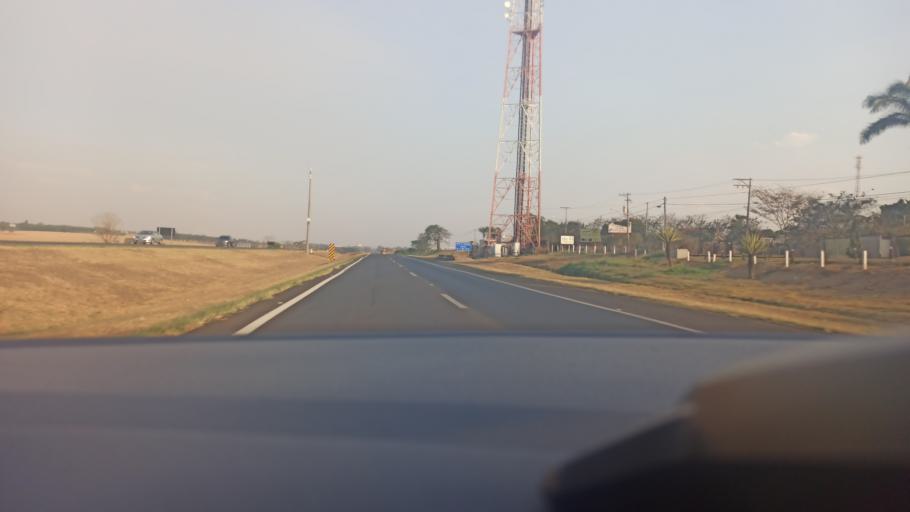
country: BR
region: Sao Paulo
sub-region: Sao Jose Do Rio Preto
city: Sao Jose do Rio Preto
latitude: -20.8895
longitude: -49.3094
